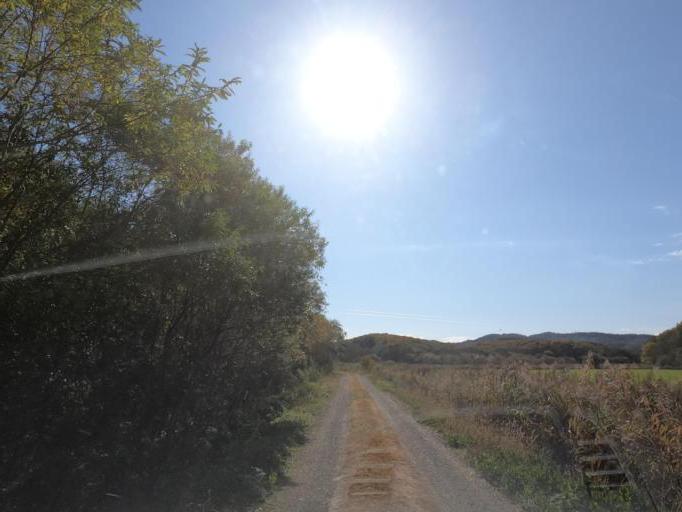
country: JP
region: Hokkaido
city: Obihiro
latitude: 42.7279
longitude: 143.4499
